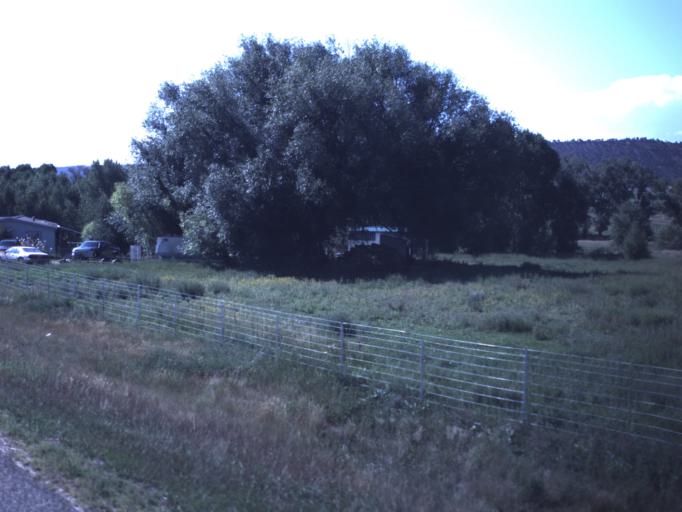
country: US
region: Utah
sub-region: Duchesne County
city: Duchesne
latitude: 40.3482
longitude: -110.7034
